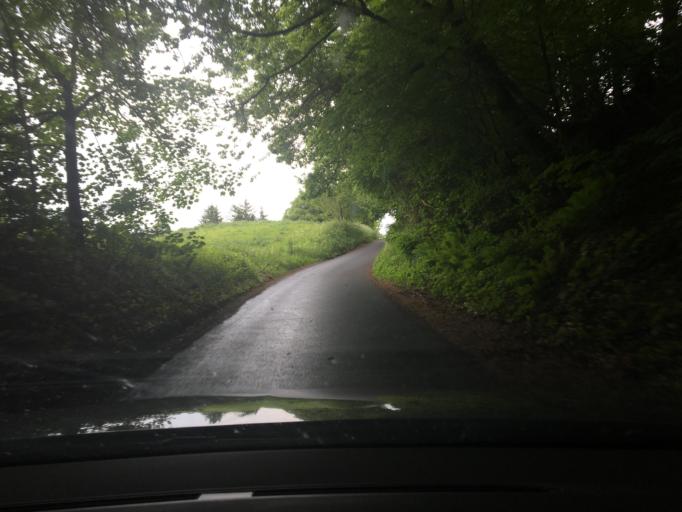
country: DK
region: South Denmark
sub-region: Fredericia Kommune
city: Taulov
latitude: 55.5547
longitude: 9.5379
